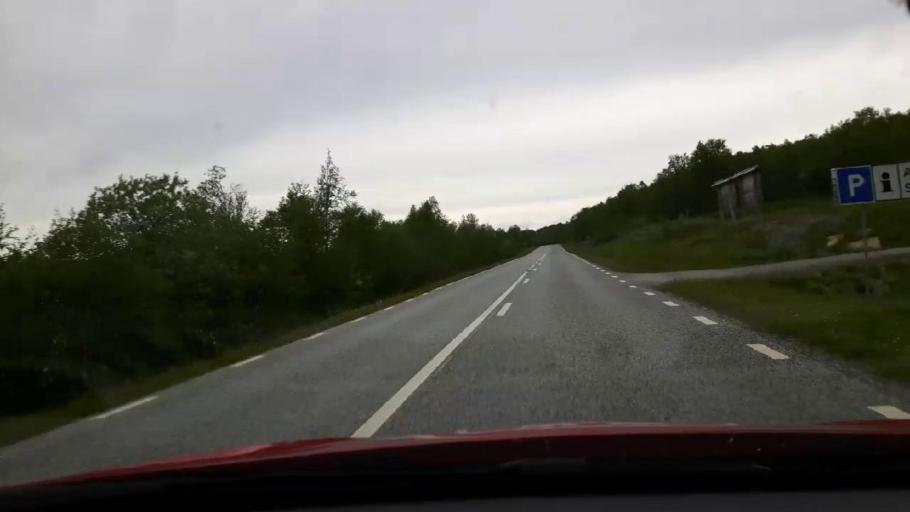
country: NO
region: Sor-Trondelag
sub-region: Tydal
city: Aas
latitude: 62.5887
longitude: 12.1946
